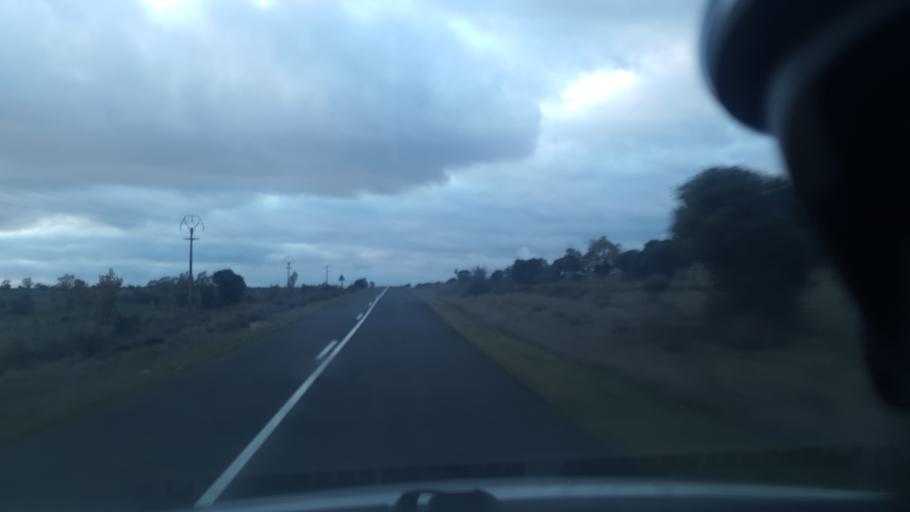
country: ES
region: Castille and Leon
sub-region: Provincia de Avila
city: Las Navas del Marques
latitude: 40.7056
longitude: -4.3347
